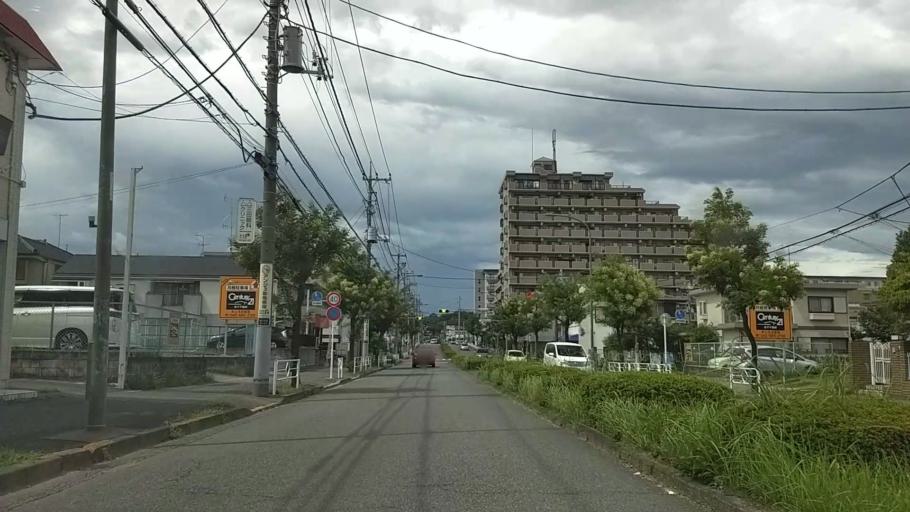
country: JP
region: Tokyo
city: Hachioji
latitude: 35.6411
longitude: 139.3080
